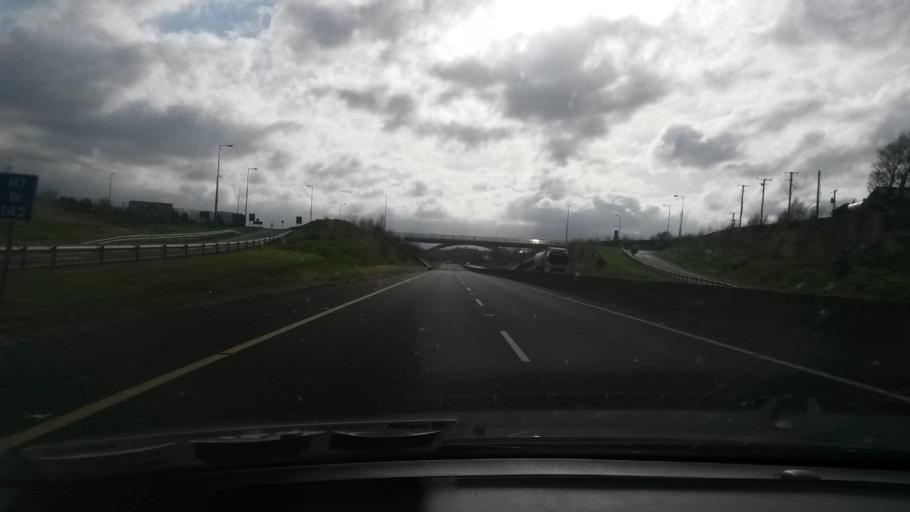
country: IE
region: Munster
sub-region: North Tipperary
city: Nenagh
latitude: 52.8603
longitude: -8.1167
